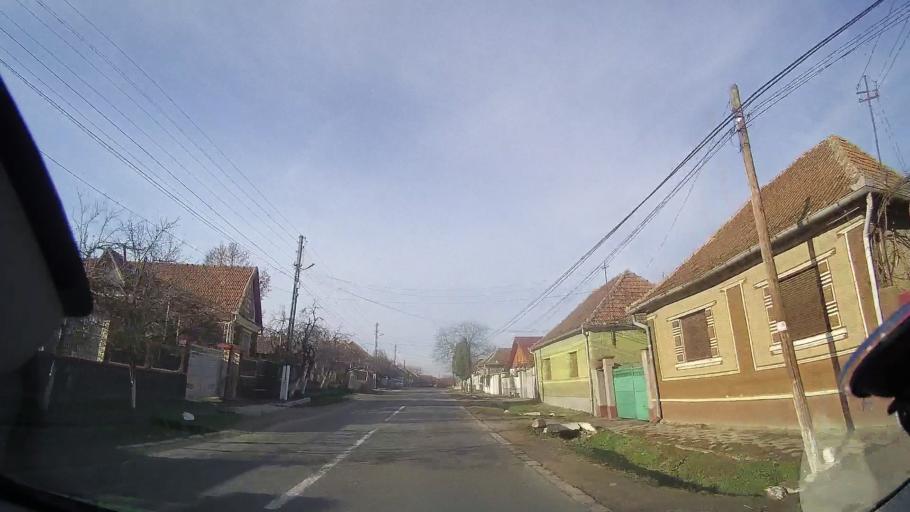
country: RO
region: Bihor
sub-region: Comuna Brusturi
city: Brusturi
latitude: 47.1446
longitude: 22.2588
